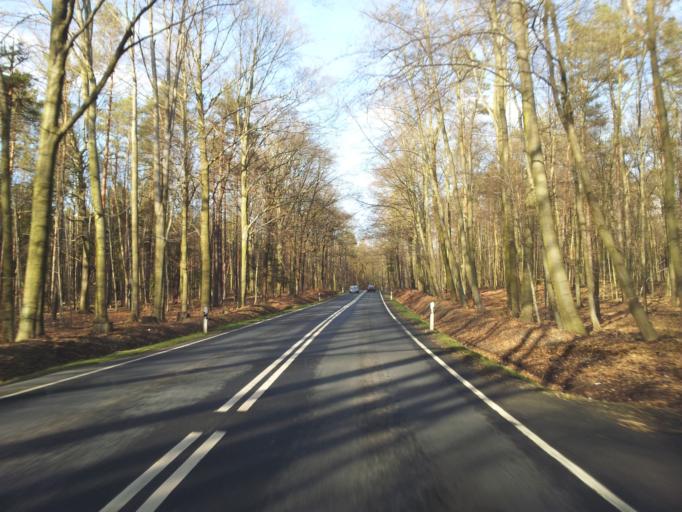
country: DE
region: Saxony
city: Laussnitz
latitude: 51.2372
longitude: 13.8487
